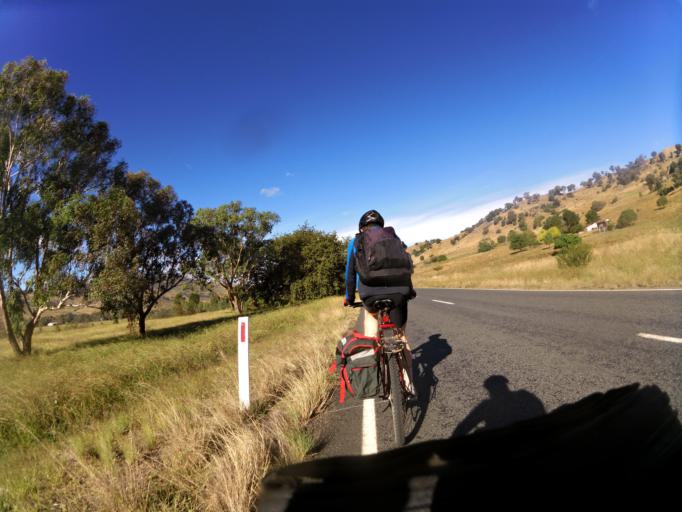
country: AU
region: New South Wales
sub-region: Greater Hume Shire
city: Holbrook
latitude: -35.9647
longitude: 147.7501
